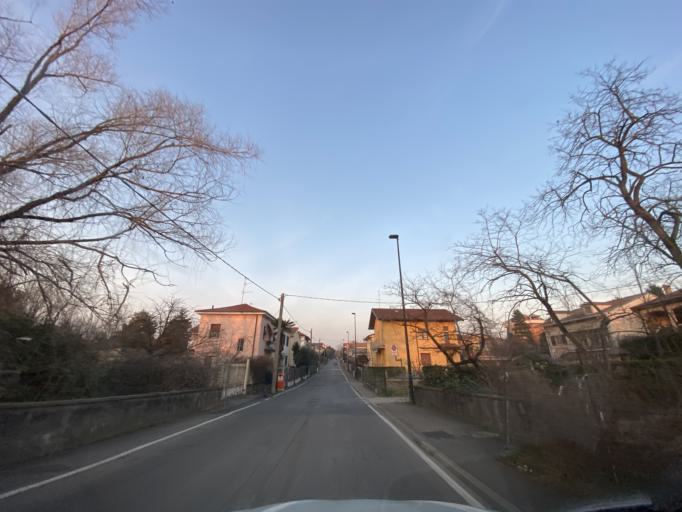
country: IT
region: Lombardy
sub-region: Provincia di Monza e Brianza
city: Villaggio del Sole
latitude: 45.6131
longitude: 9.1057
